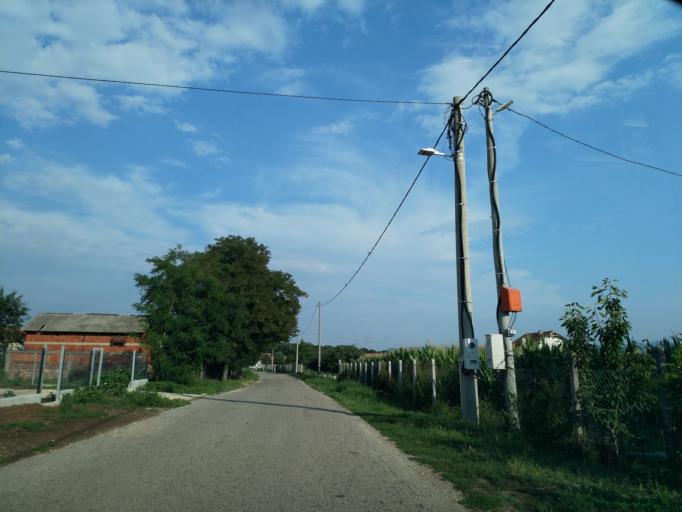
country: RS
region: Central Serbia
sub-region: Pomoravski Okrug
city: Jagodina
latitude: 43.9863
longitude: 21.2150
